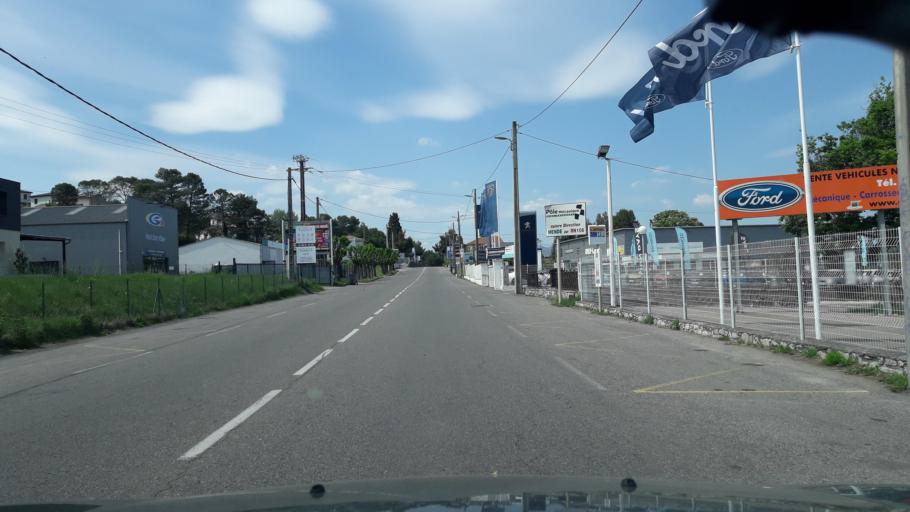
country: FR
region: Languedoc-Roussillon
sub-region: Departement du Gard
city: Saint-Hilaire-de-Brethmas
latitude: 44.1101
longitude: 4.1116
